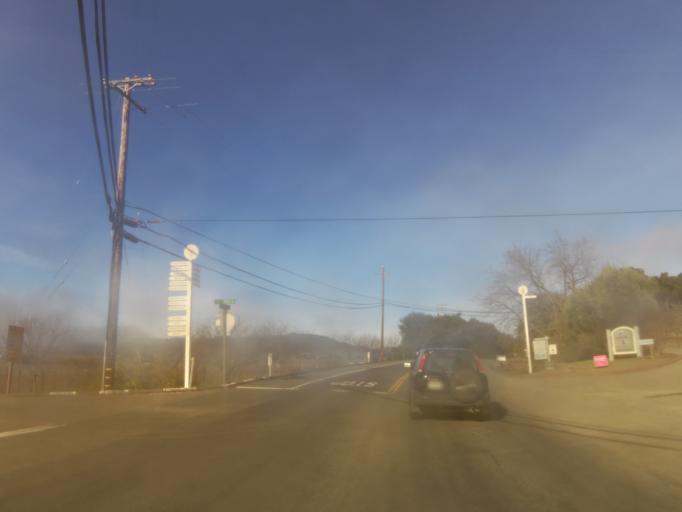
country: US
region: California
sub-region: Sonoma County
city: Healdsburg
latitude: 38.6548
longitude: -122.9221
